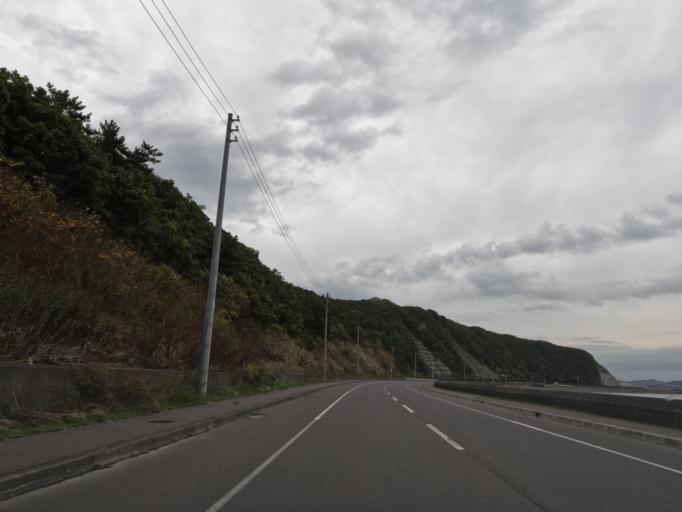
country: JP
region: Hokkaido
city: Muroran
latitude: 42.3765
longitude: 140.9102
